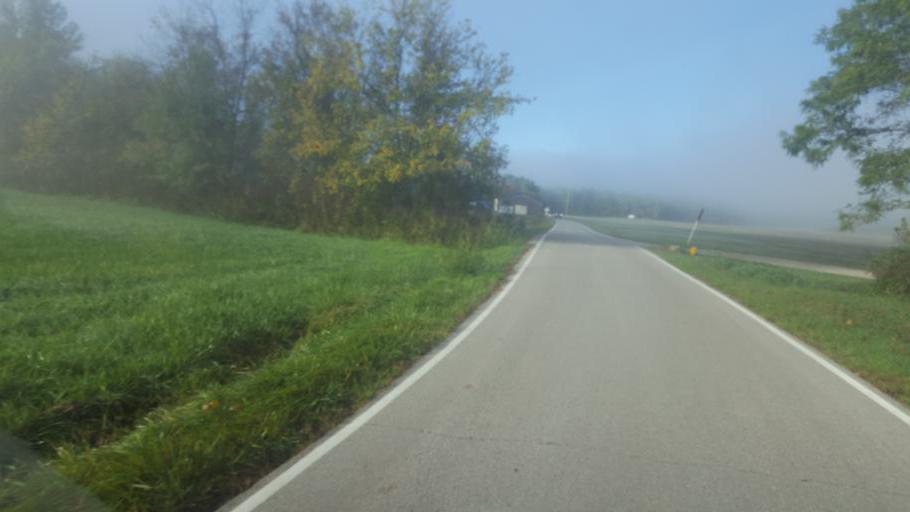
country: US
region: Ohio
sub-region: Adams County
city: Manchester
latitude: 38.5095
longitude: -83.5412
